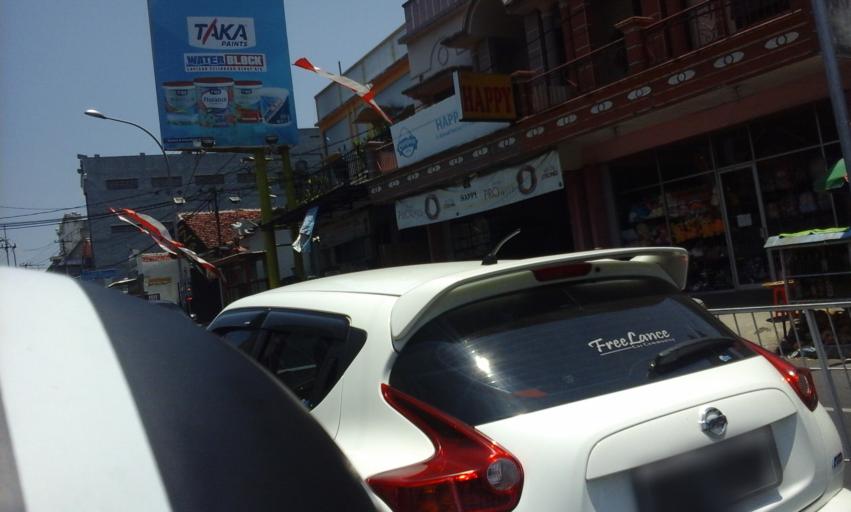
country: ID
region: East Java
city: Kepatihan
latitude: -8.1763
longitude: 113.7045
